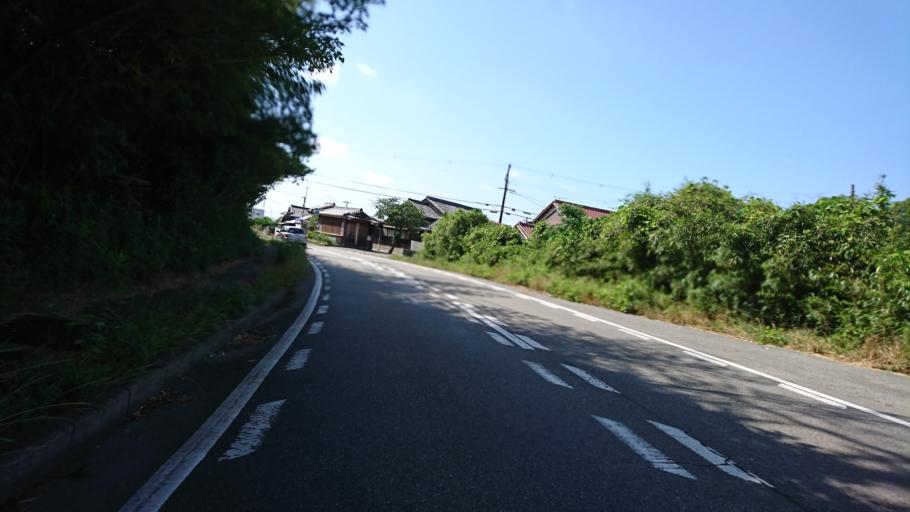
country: JP
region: Hyogo
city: Shirahamacho-usazakiminami
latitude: 34.7978
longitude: 134.7430
